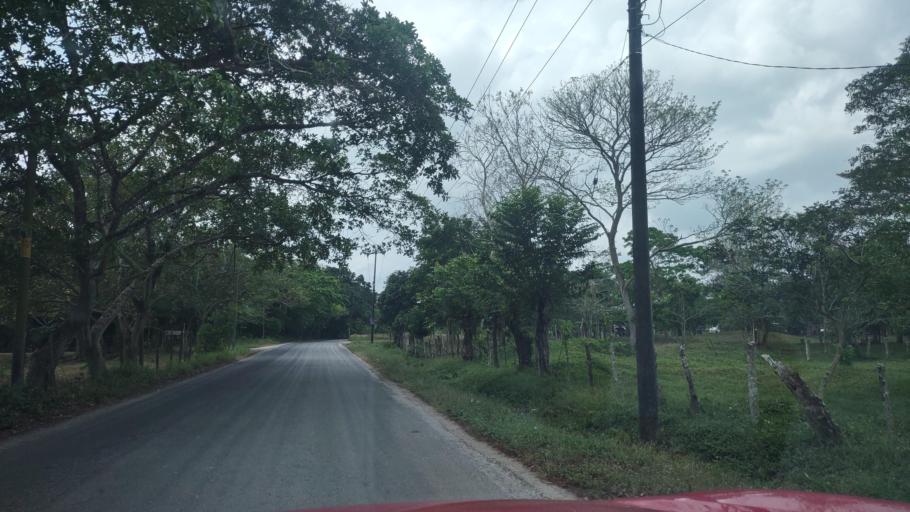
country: MX
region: Veracruz
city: Las Choapas
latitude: 17.9647
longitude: -94.1109
